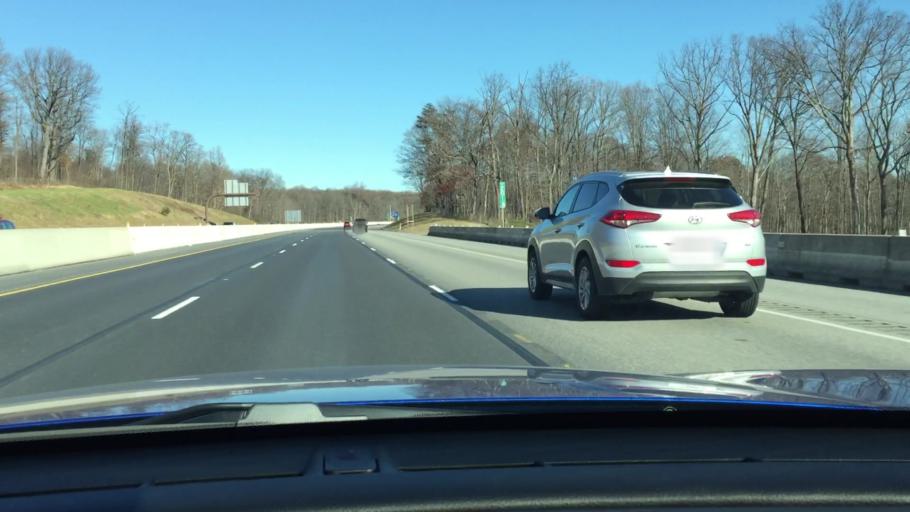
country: US
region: Pennsylvania
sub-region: Franklin County
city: Doylestown
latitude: 40.1615
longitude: -77.6086
